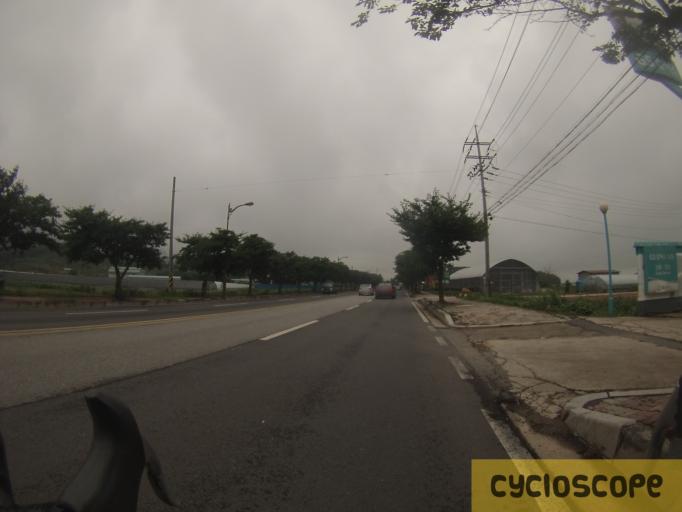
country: KR
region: Chungcheongnam-do
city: Asan
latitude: 36.8044
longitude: 126.9198
